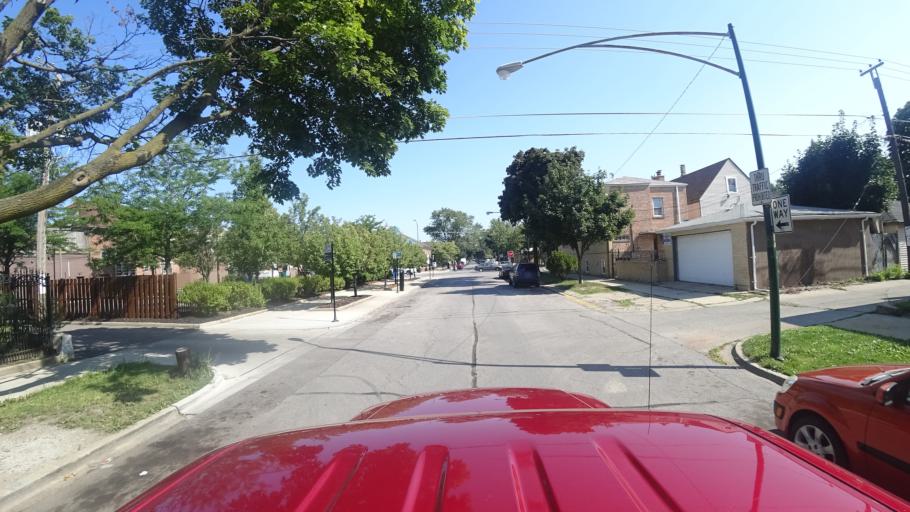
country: US
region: Illinois
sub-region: Cook County
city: Hometown
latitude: 41.7932
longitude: -87.6926
